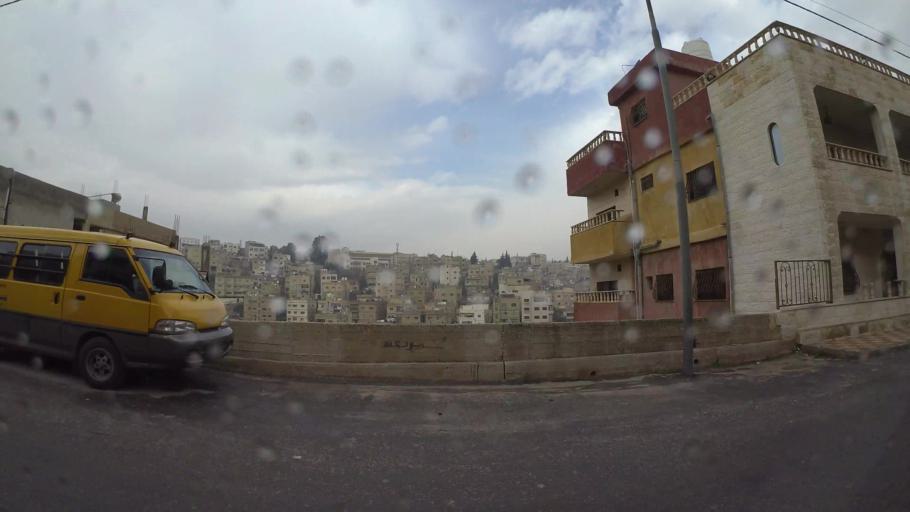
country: JO
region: Amman
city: Amman
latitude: 31.9603
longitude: 35.9356
